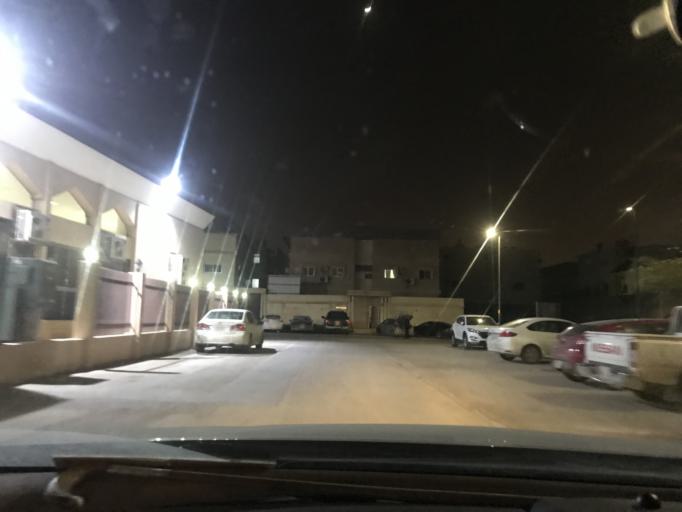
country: SA
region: Ar Riyad
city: Riyadh
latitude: 24.7462
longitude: 46.7615
